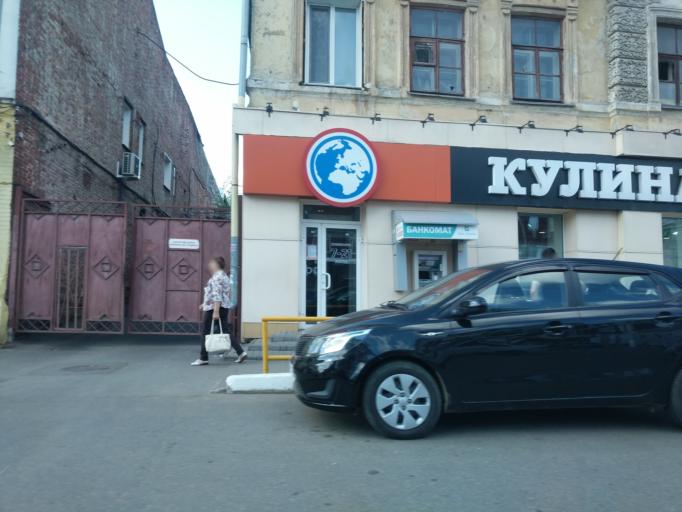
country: RU
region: Kirov
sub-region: Kirovo-Chepetskiy Rayon
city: Kirov
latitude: 58.6044
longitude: 49.6808
